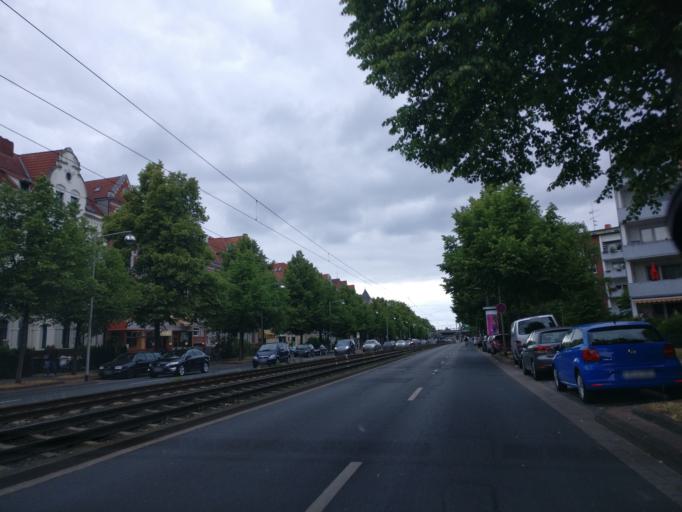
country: DE
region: Lower Saxony
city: Laatzen
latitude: 52.3395
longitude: 9.7676
